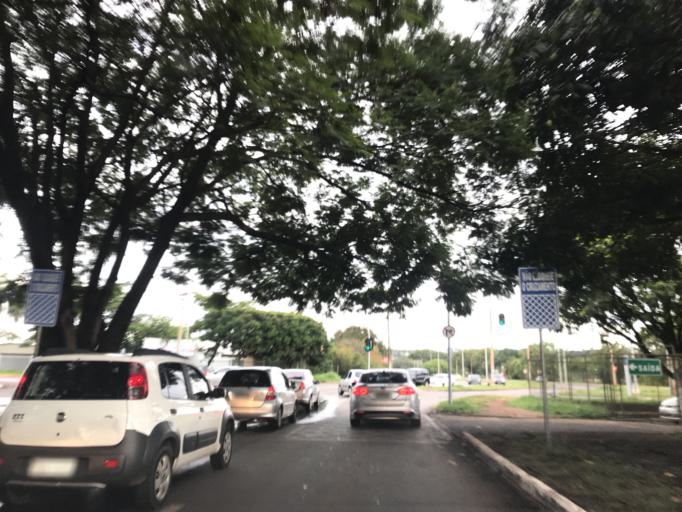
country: BR
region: Federal District
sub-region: Brasilia
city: Brasilia
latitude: -15.8175
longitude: -47.9198
